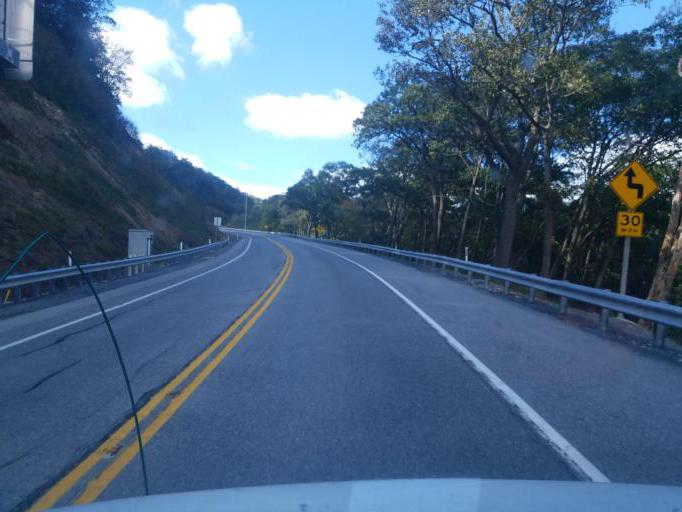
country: US
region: Pennsylvania
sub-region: Fulton County
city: McConnellsburg
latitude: 40.0169
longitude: -78.1319
